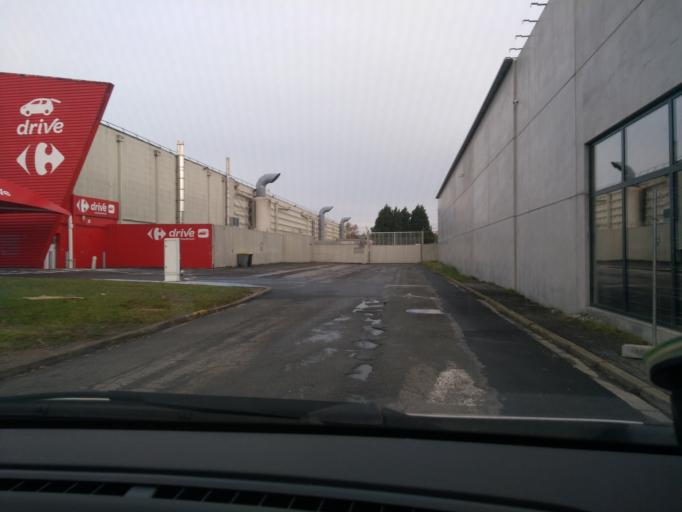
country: FR
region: Nord-Pas-de-Calais
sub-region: Departement du Nord
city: Maubeuge
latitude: 50.2895
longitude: 3.9689
